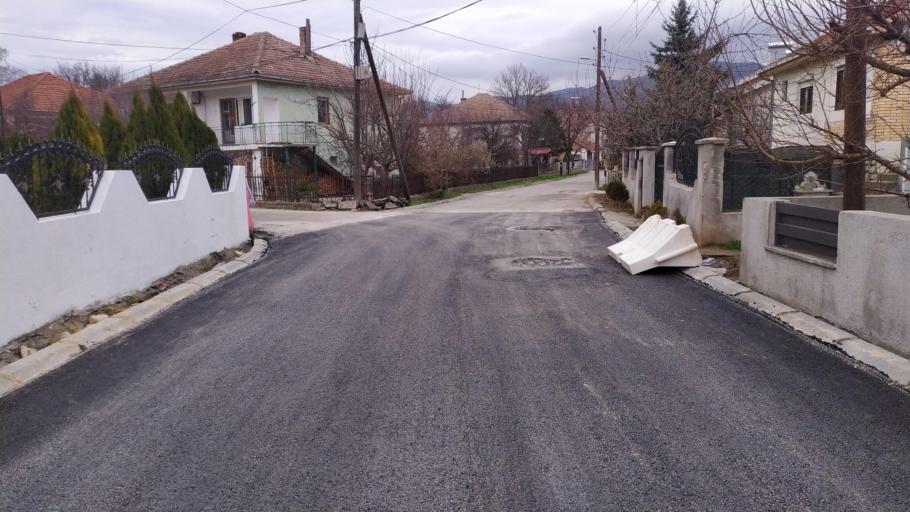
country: MK
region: Demir Kapija
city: Demir Kapija
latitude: 41.4091
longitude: 22.2391
